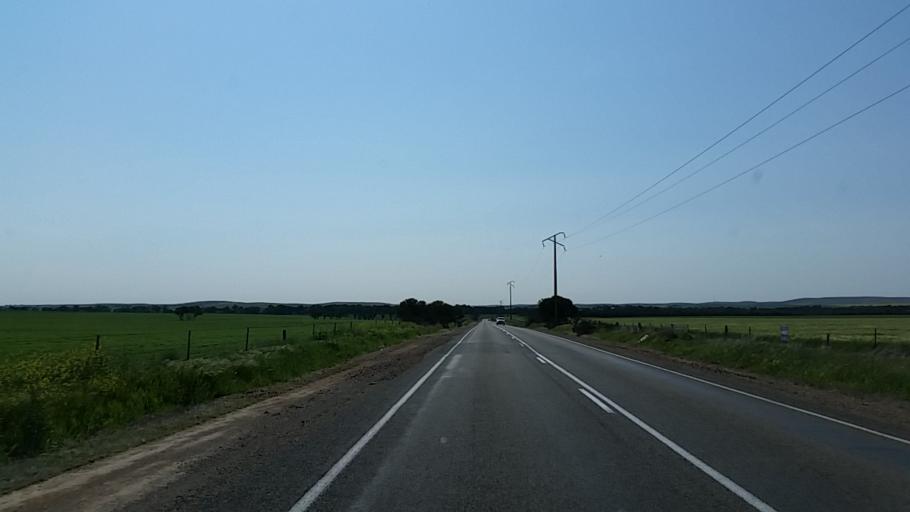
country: AU
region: South Australia
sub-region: Port Pirie City and Dists
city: Crystal Brook
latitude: -33.2712
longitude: 138.3165
